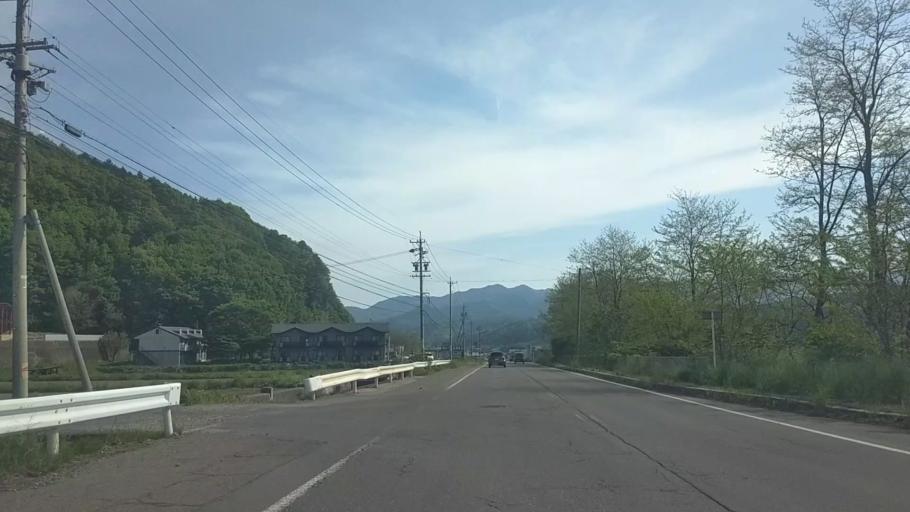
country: JP
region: Nagano
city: Saku
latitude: 36.0638
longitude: 138.4712
